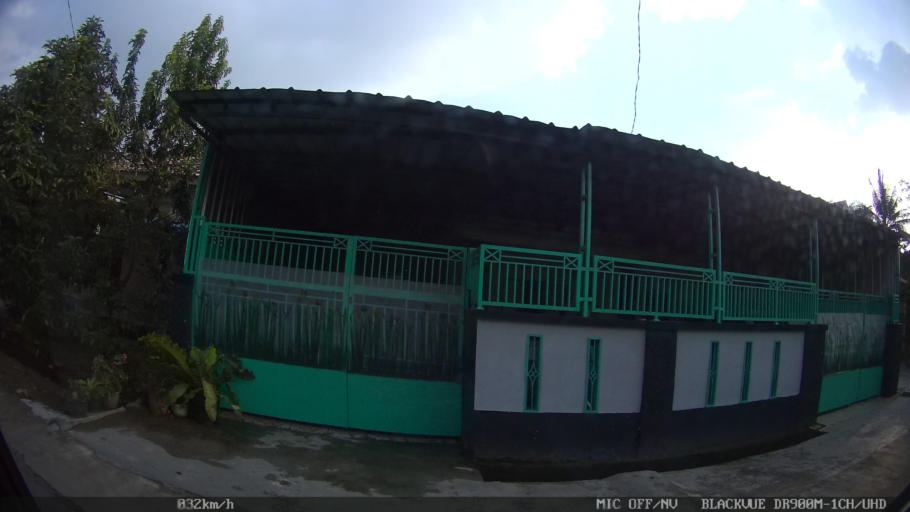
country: ID
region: Lampung
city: Panjang
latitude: -5.3932
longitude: 105.3517
